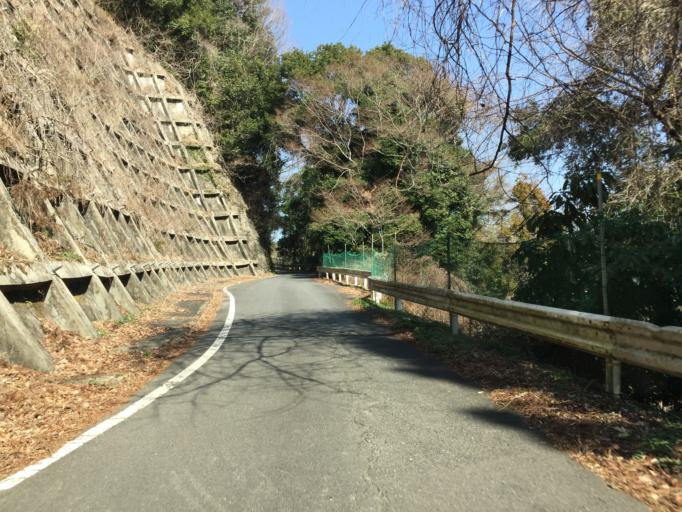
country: JP
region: Ibaraki
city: Kitaibaraki
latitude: 36.9327
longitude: 140.7314
